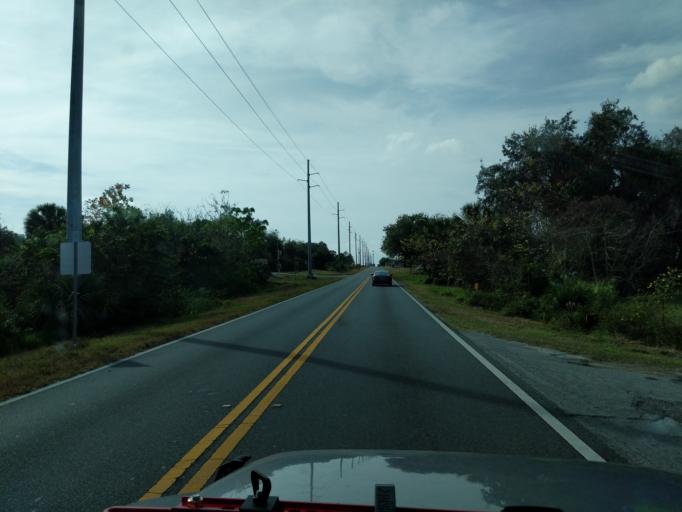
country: US
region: Florida
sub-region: Lake County
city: Mount Dora
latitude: 28.8071
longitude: -81.6767
